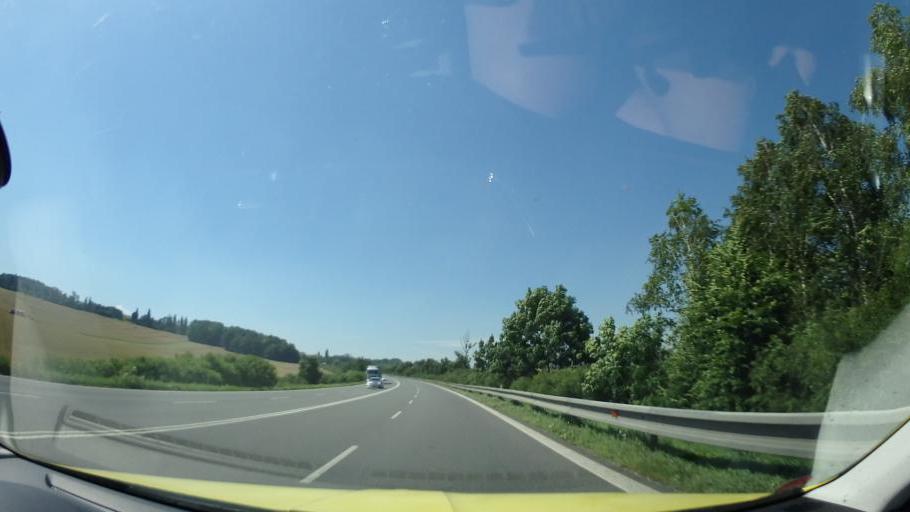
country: CZ
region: Olomoucky
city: Hustopece Nad Becvou
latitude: 49.5613
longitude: 17.8986
